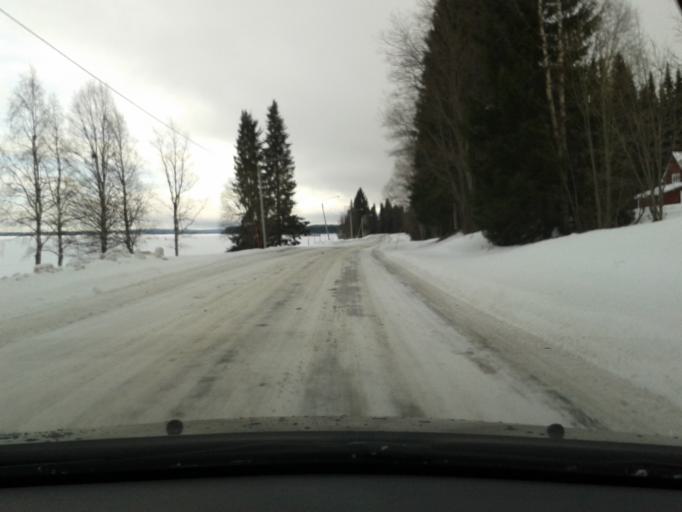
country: SE
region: Vaesterbotten
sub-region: Vilhelmina Kommun
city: Sjoberg
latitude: 64.6659
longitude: 16.3047
